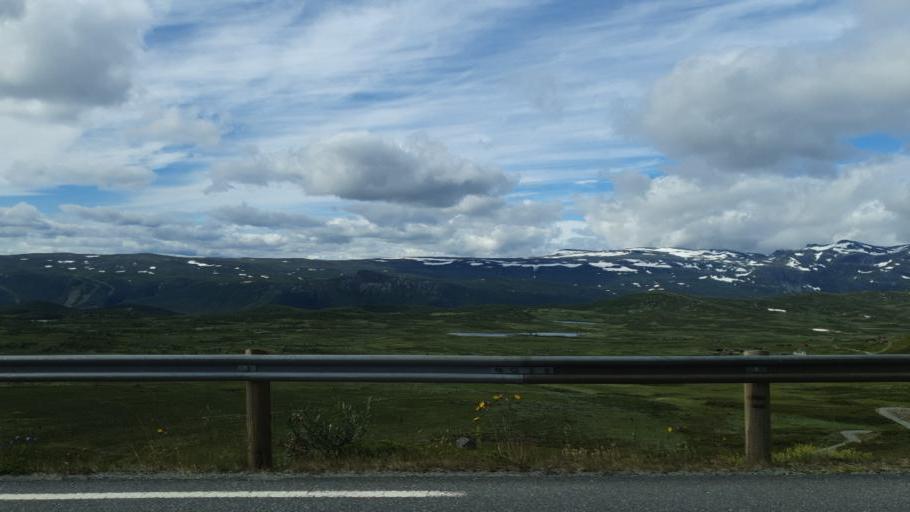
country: NO
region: Oppland
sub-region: Vestre Slidre
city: Slidre
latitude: 61.2786
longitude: 8.8489
